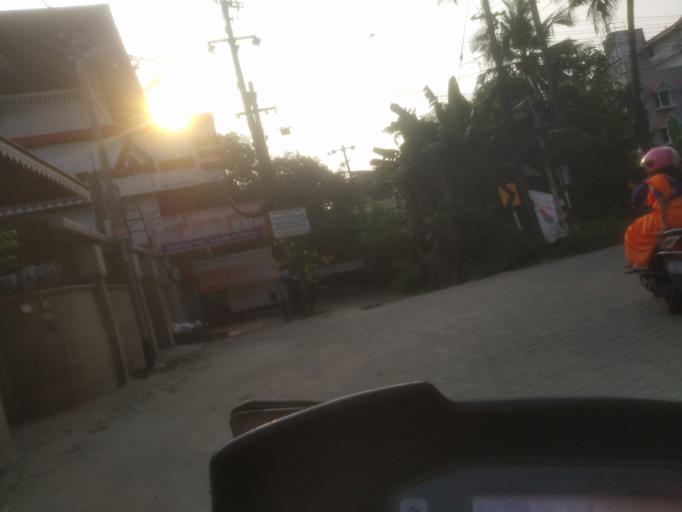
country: IN
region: Kerala
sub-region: Alappuzha
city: Arukutti
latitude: 9.9417
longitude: 76.3449
